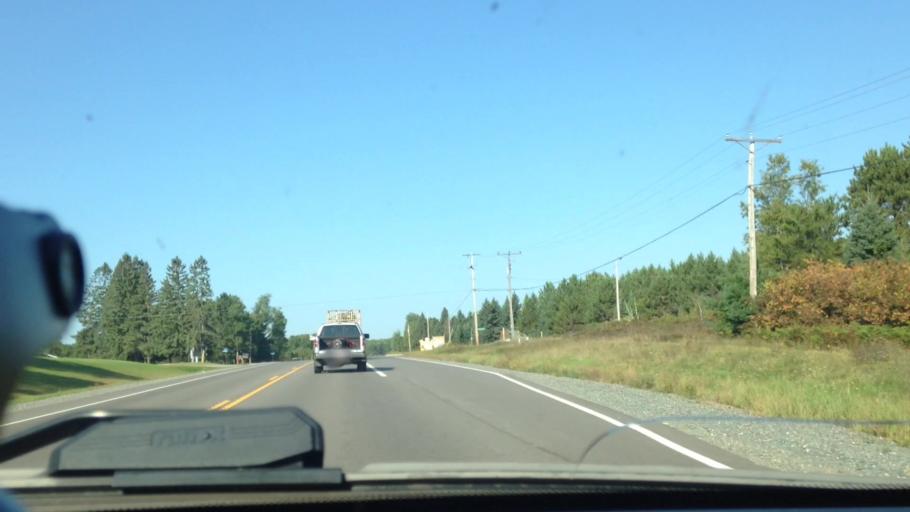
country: US
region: Michigan
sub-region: Dickinson County
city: Iron Mountain
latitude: 45.8760
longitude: -88.1067
